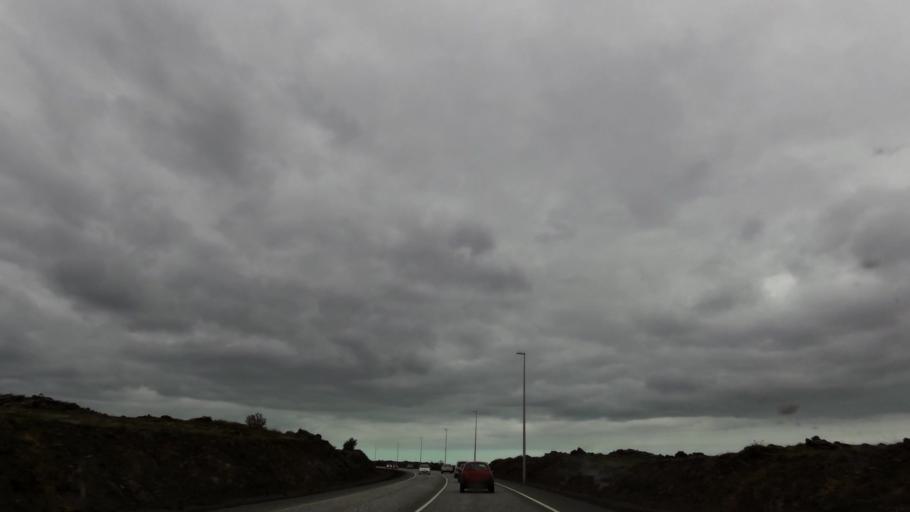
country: IS
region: Capital Region
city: Hafnarfjoerdur
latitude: 64.0883
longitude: -21.9616
